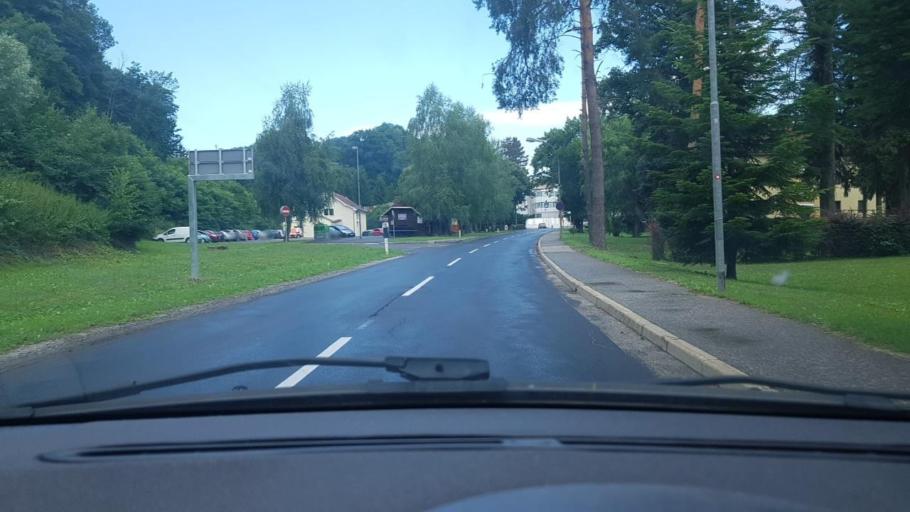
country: AT
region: Styria
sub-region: Politischer Bezirk Suedoststeiermark
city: Mureck
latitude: 46.6969
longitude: 15.7378
